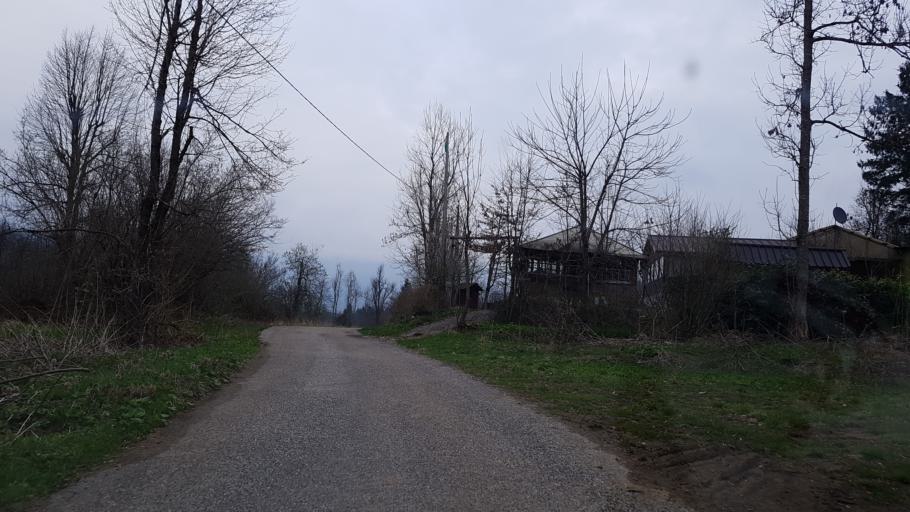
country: IT
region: Friuli Venezia Giulia
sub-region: Provincia di Udine
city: Faedis
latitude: 46.1946
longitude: 13.3991
